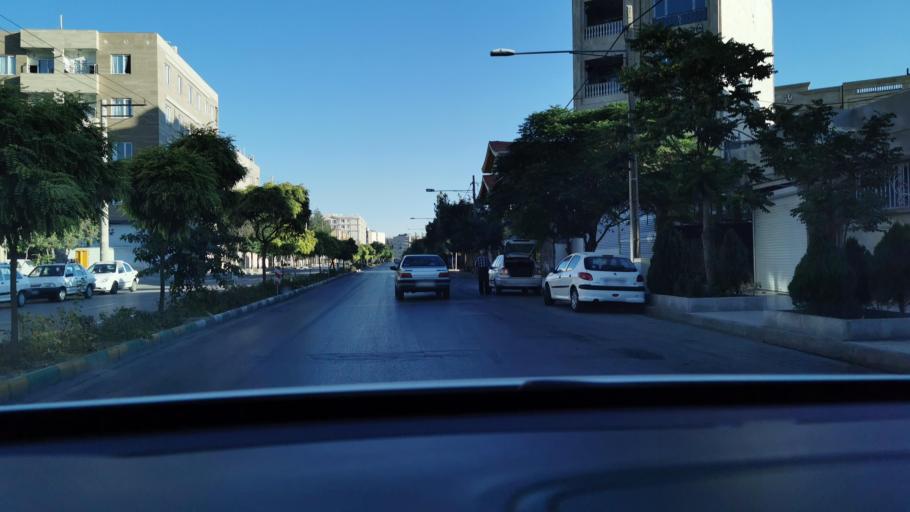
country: IR
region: Razavi Khorasan
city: Mashhad
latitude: 36.3571
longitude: 59.4868
